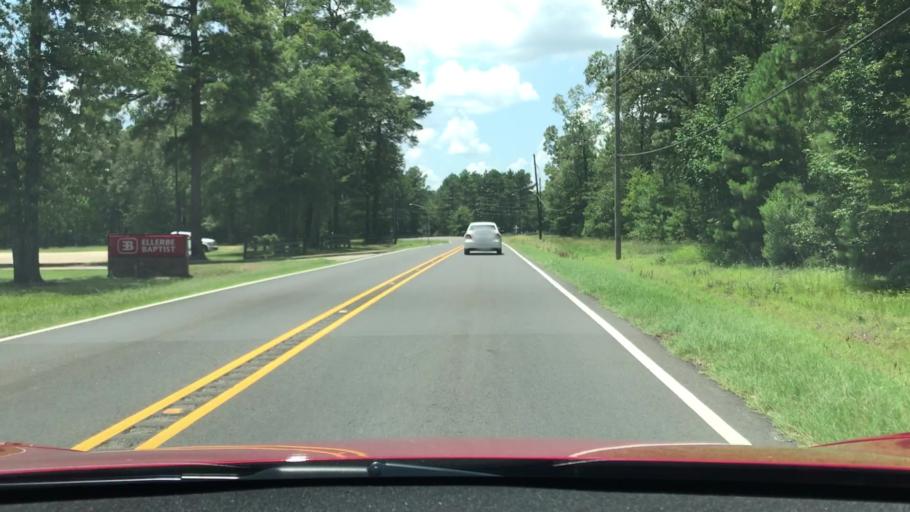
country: US
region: Louisiana
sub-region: Bossier Parish
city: Bossier City
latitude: 32.3649
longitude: -93.6903
